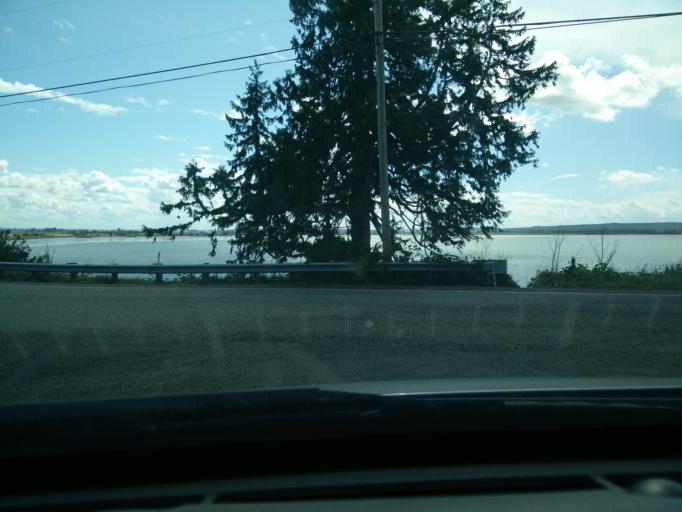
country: US
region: Washington
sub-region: Skagit County
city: Anacortes
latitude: 48.4808
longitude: -122.4749
